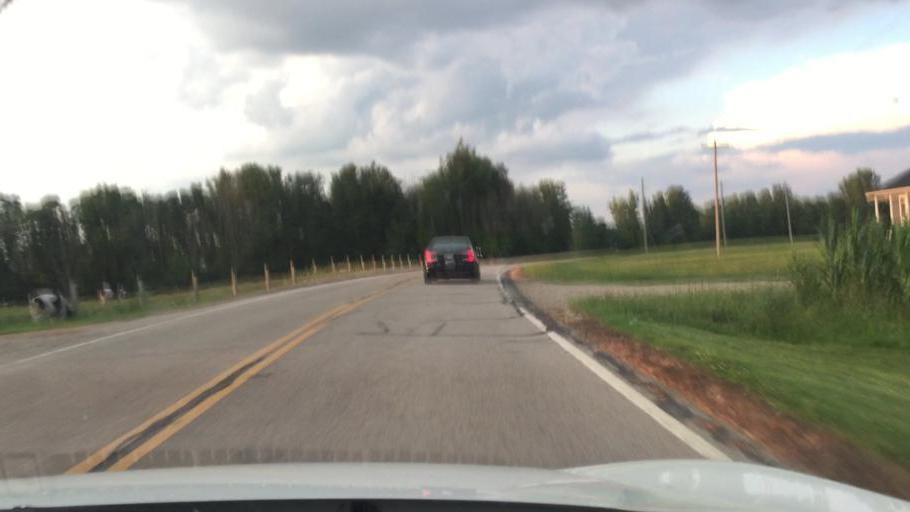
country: US
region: Ohio
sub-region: Champaign County
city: Mechanicsburg
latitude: 40.0399
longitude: -83.5684
